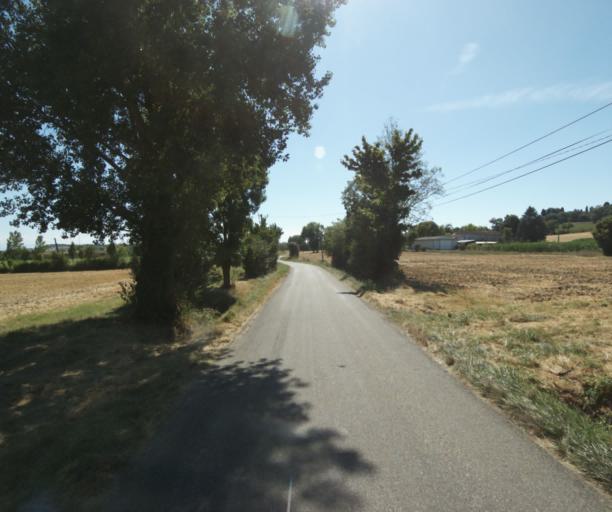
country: FR
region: Midi-Pyrenees
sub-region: Departement de la Haute-Garonne
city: Saint-Felix-Lauragais
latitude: 43.4930
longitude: 1.9360
